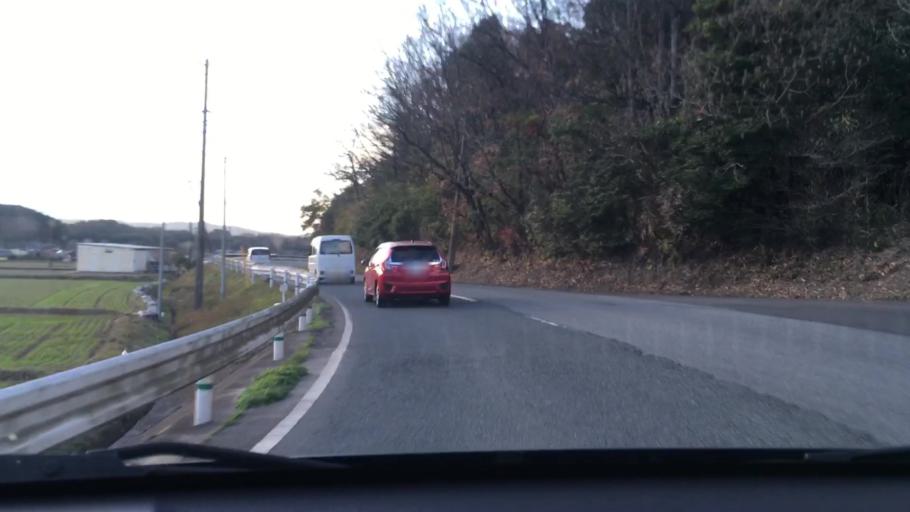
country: JP
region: Oita
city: Bungo-Takada-shi
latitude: 33.5079
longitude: 131.3611
